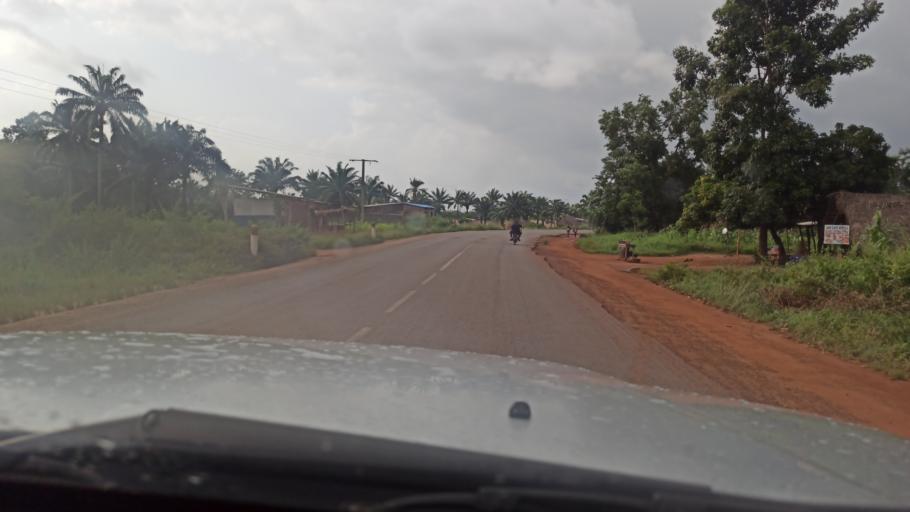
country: BJ
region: Queme
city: Porto-Novo
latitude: 6.5699
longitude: 2.5770
